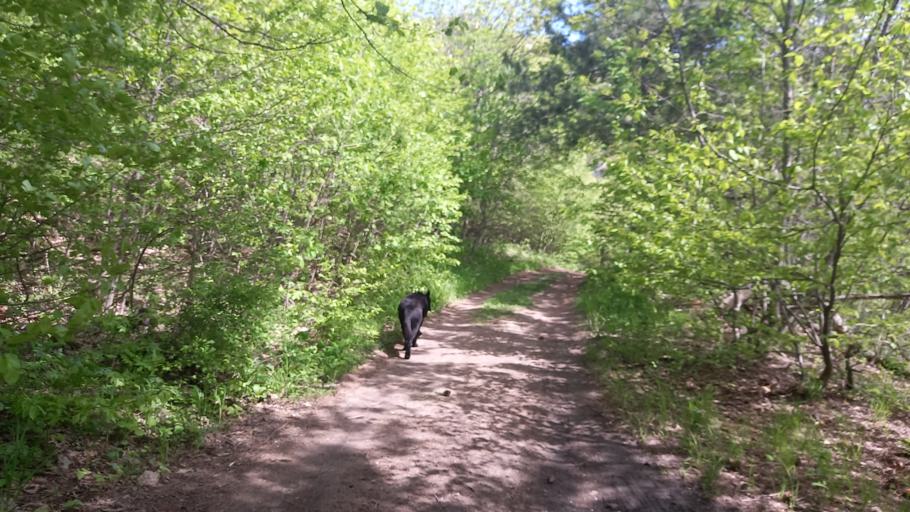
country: RU
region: Stavropol'skiy
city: Pyatigorsk
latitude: 44.0887
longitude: 43.0294
